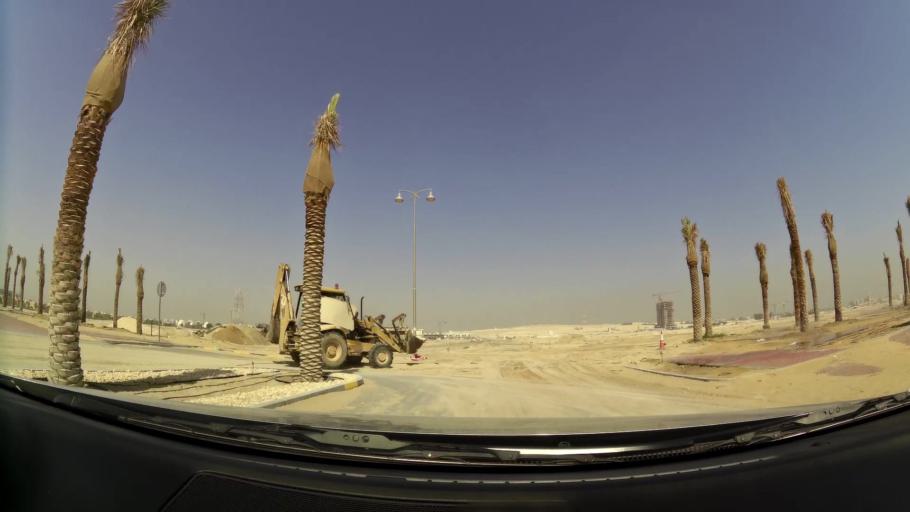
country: AE
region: Dubai
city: Dubai
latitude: 25.0265
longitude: 55.1472
